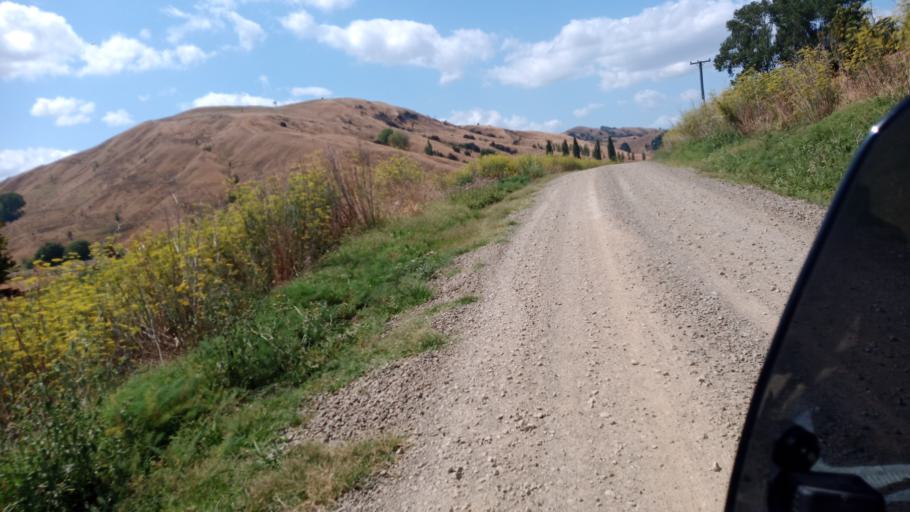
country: NZ
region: Gisborne
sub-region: Gisborne District
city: Gisborne
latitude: -38.4794
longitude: 177.8396
